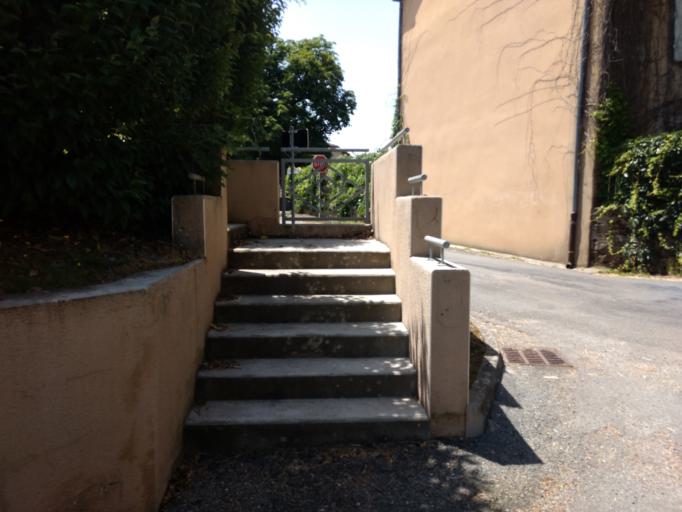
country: FR
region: Midi-Pyrenees
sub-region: Departement de l'Aveyron
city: Livinhac-le-Haut
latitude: 44.6520
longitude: 2.2546
